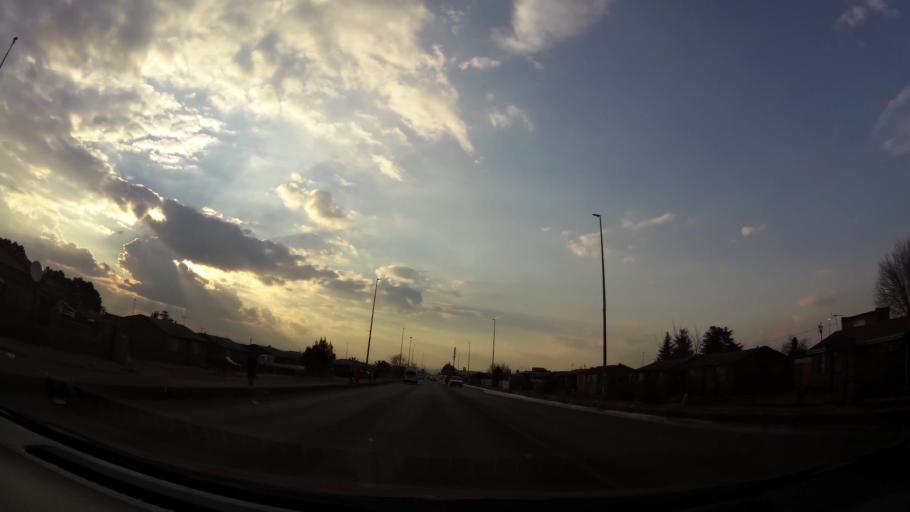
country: ZA
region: Gauteng
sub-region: City of Johannesburg Metropolitan Municipality
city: Orange Farm
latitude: -26.5756
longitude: 27.8400
